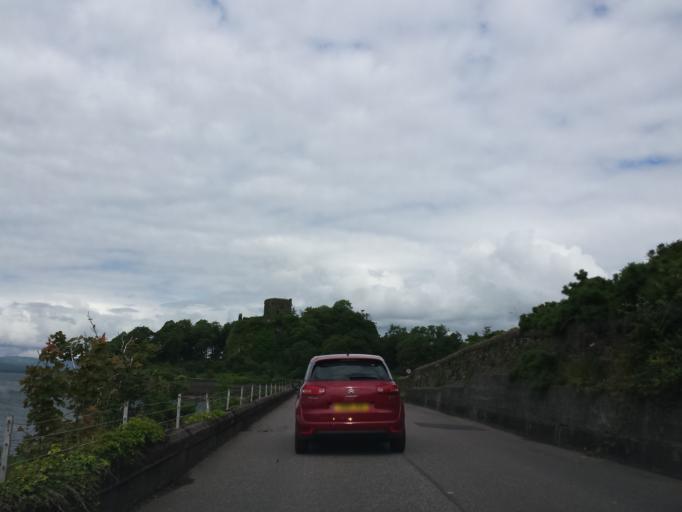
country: GB
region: Scotland
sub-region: Argyll and Bute
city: Oban
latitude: 56.4233
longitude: -5.4839
